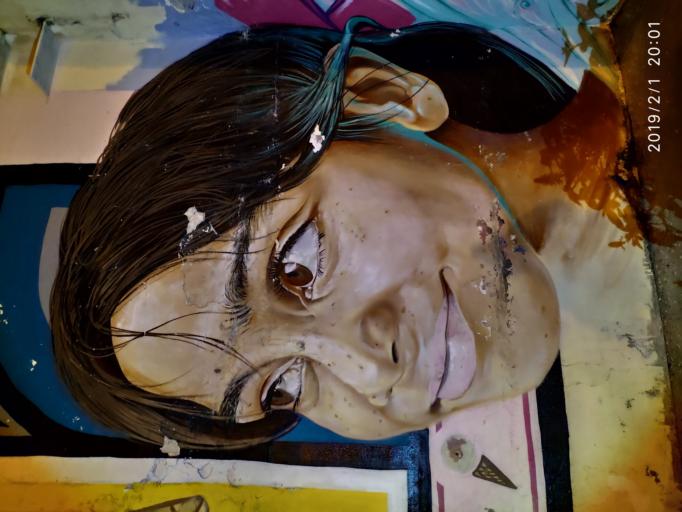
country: ES
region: Andalusia
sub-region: Provincia de Malaga
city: Malaga
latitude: 36.7261
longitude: -4.4153
